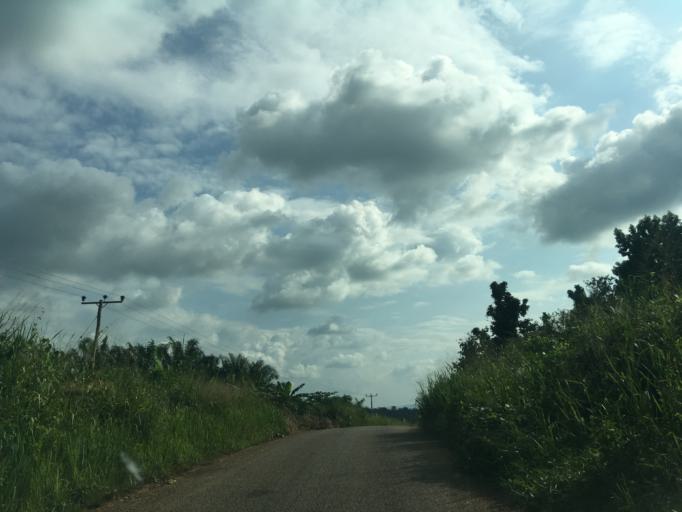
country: GH
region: Western
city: Bibiani
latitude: 6.7883
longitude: -2.5391
